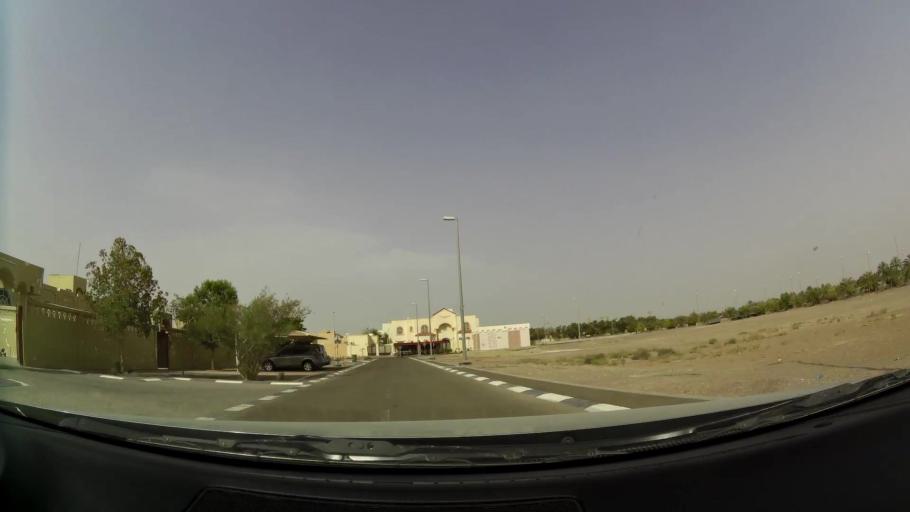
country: AE
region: Abu Dhabi
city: Al Ain
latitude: 24.1776
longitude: 55.6046
